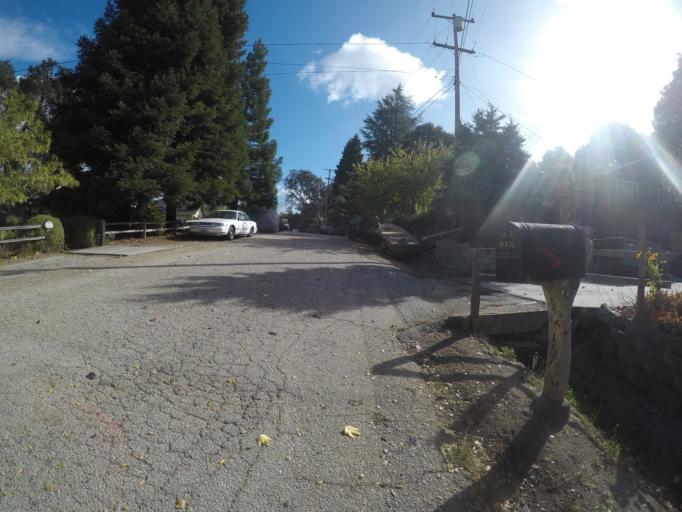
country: US
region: California
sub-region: Santa Cruz County
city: Scotts Valley
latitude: 37.0578
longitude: -122.0014
